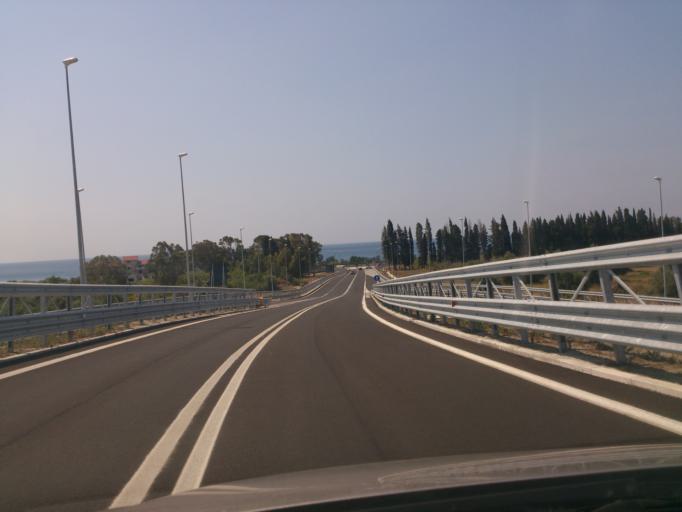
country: IT
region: Calabria
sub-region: Provincia di Reggio Calabria
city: Marina di Gioiosa Ionica
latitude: 38.3100
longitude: 16.3537
